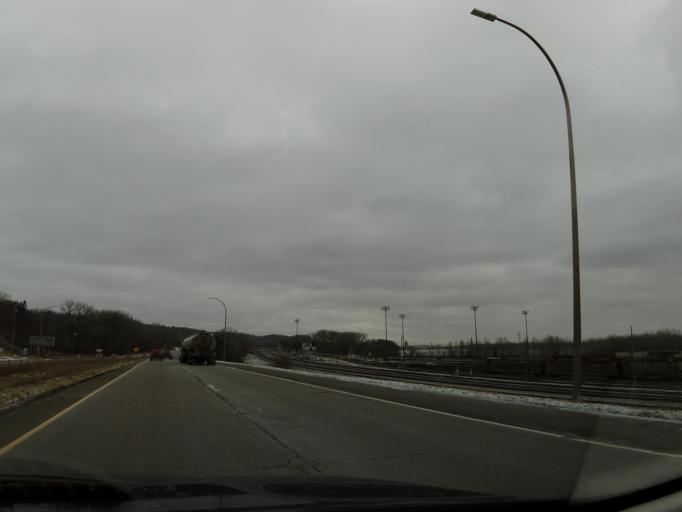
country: US
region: Minnesota
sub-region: Ramsey County
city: Maplewood
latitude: 44.9342
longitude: -93.0287
